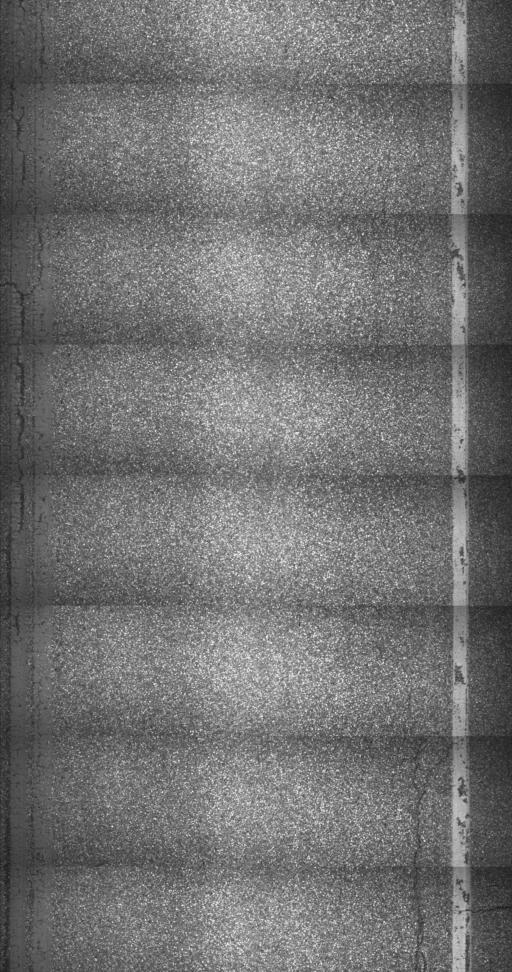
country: US
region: Vermont
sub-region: Windsor County
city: Woodstock
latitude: 43.4995
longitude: -72.7159
